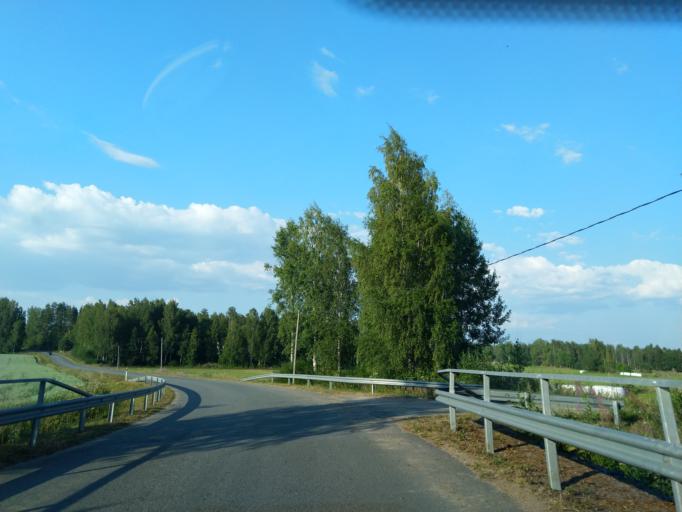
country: FI
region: Satakunta
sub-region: Pohjois-Satakunta
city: Honkajoki
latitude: 61.8153
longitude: 22.1968
